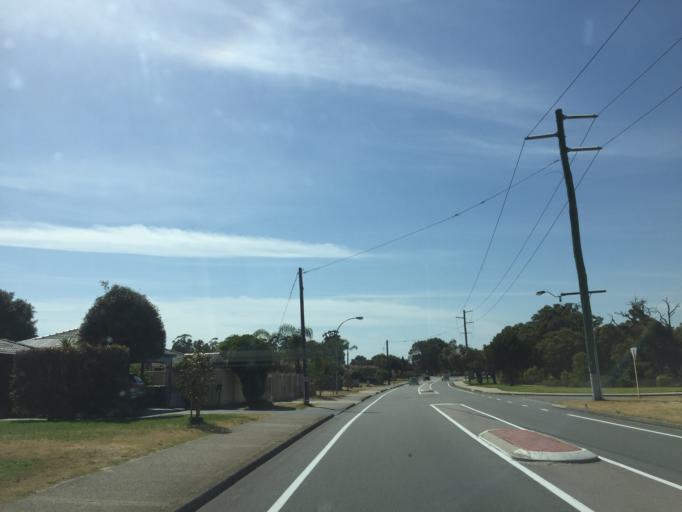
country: AU
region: Western Australia
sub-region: Gosnells
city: Thornlie
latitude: -32.0735
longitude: 115.9592
